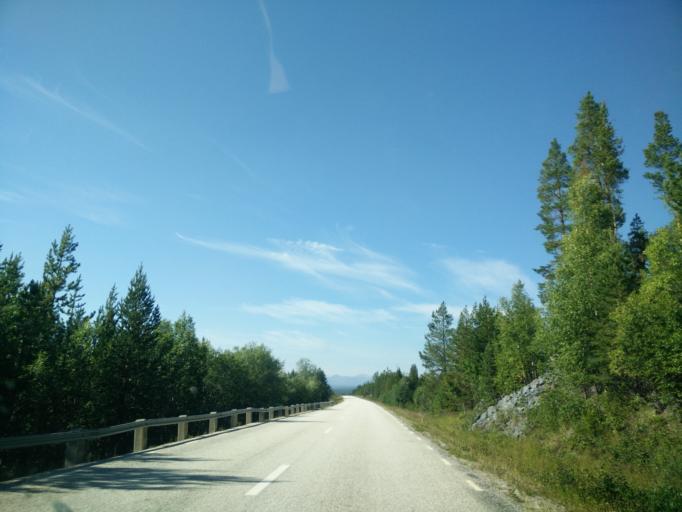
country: SE
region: Jaemtland
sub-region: Are Kommun
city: Jarpen
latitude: 62.8048
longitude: 13.5449
